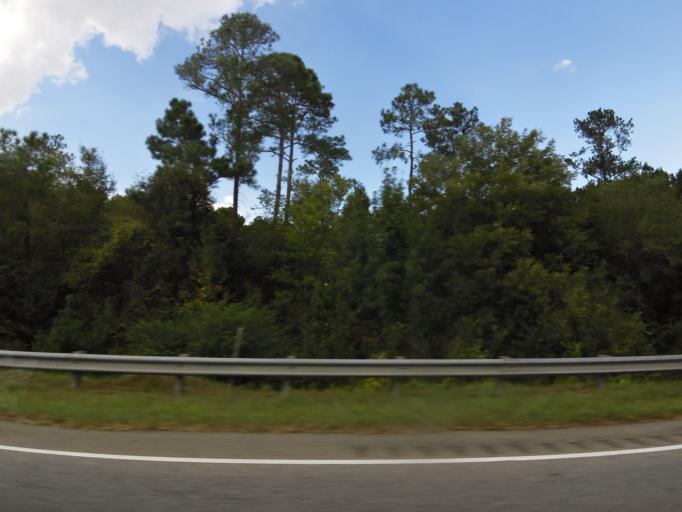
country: US
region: Georgia
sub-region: Brooks County
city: Quitman
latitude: 30.7867
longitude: -83.5161
